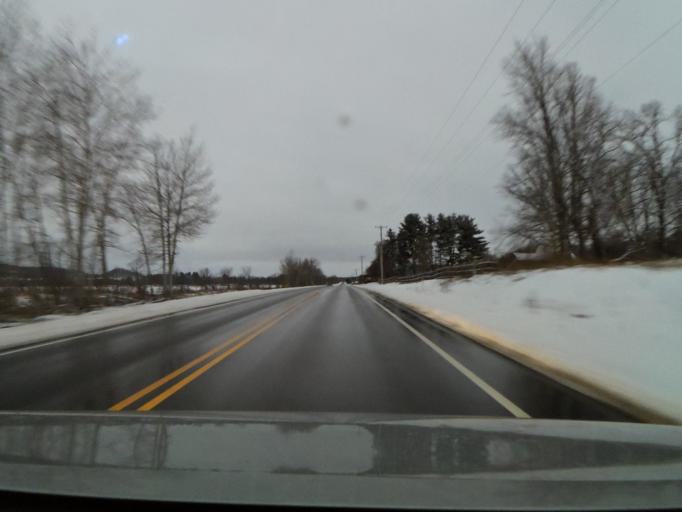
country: US
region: Wisconsin
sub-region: Dunn County
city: Boyceville
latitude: 44.9536
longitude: -92.0560
